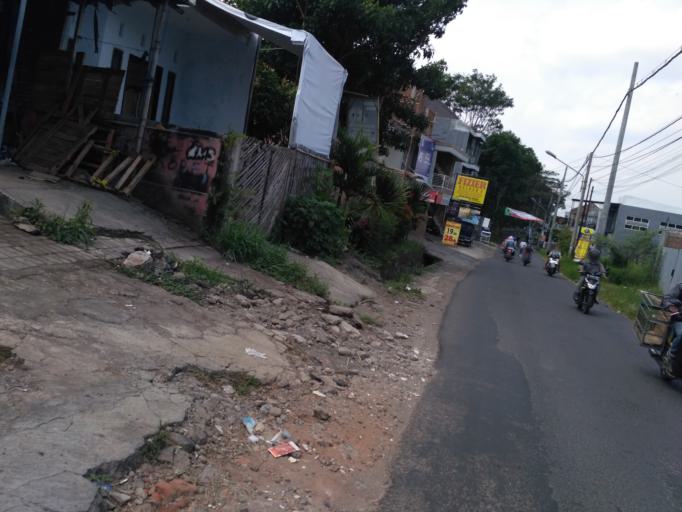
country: ID
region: East Java
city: Malang
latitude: -7.9246
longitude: 112.6039
